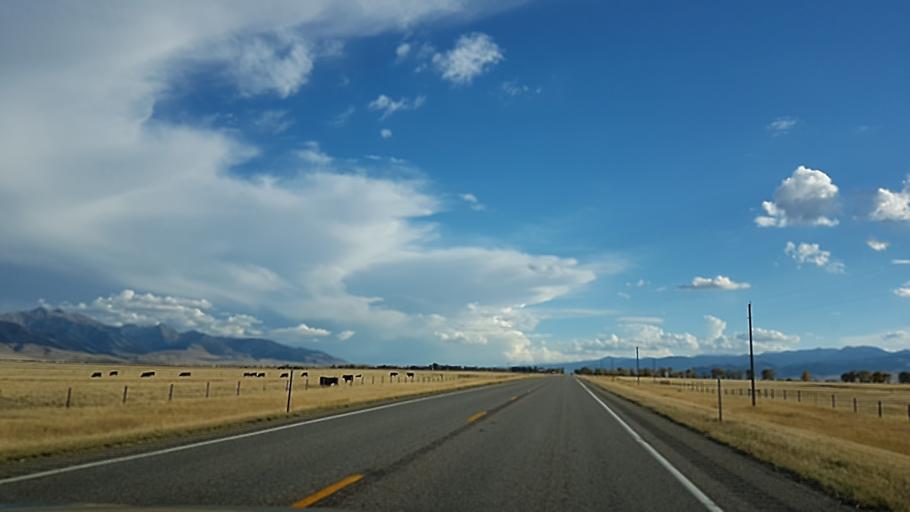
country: US
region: Montana
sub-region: Madison County
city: Virginia City
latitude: 45.2198
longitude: -111.6789
